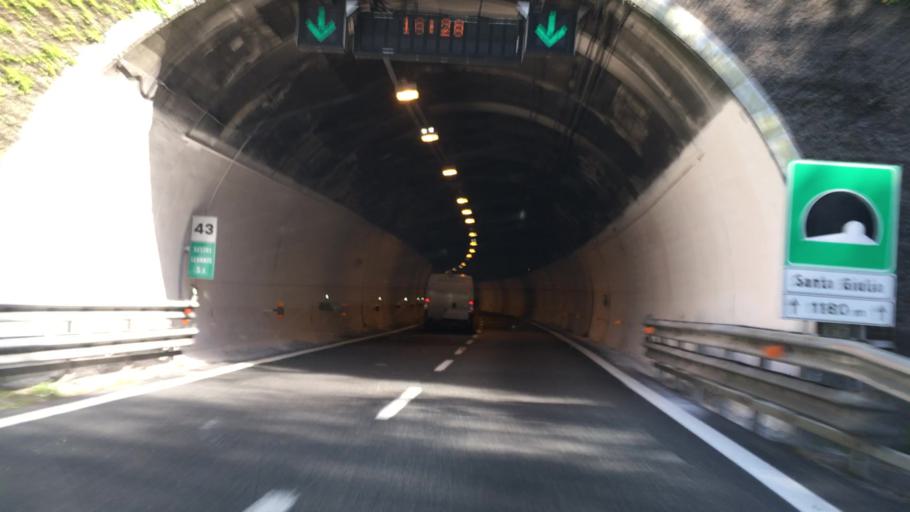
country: IT
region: Liguria
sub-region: Provincia di Genova
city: Lavagna
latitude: 44.3064
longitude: 9.3676
